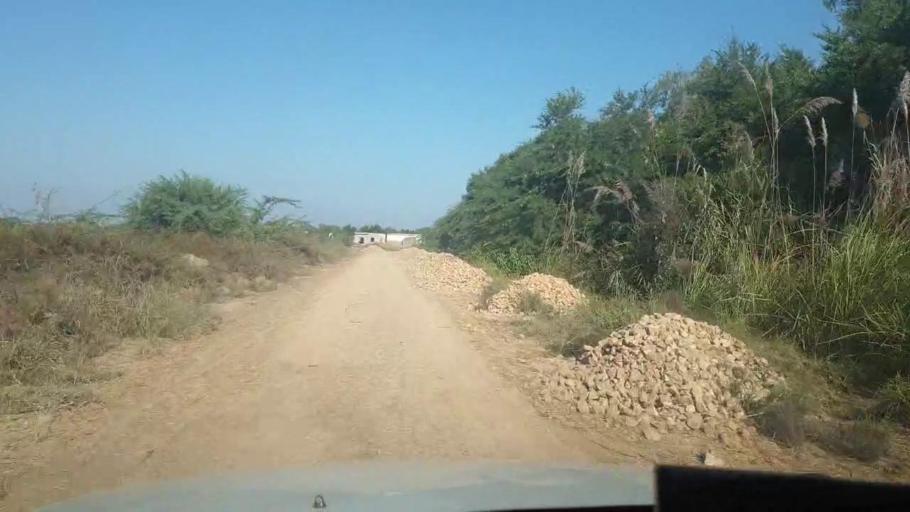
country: PK
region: Sindh
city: Mirpur Sakro
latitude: 24.5015
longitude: 67.6233
